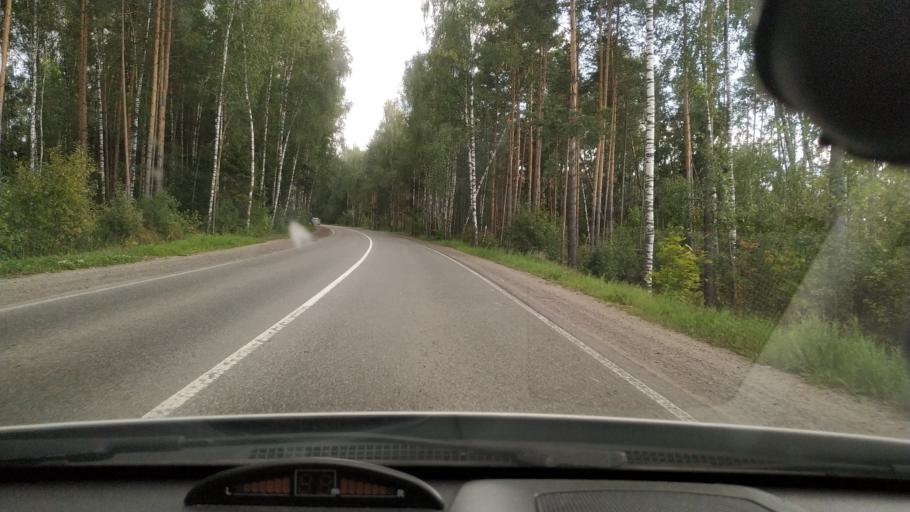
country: RU
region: Moskovskaya
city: Zheleznodorozhnyy
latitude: 55.7817
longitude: 38.0403
